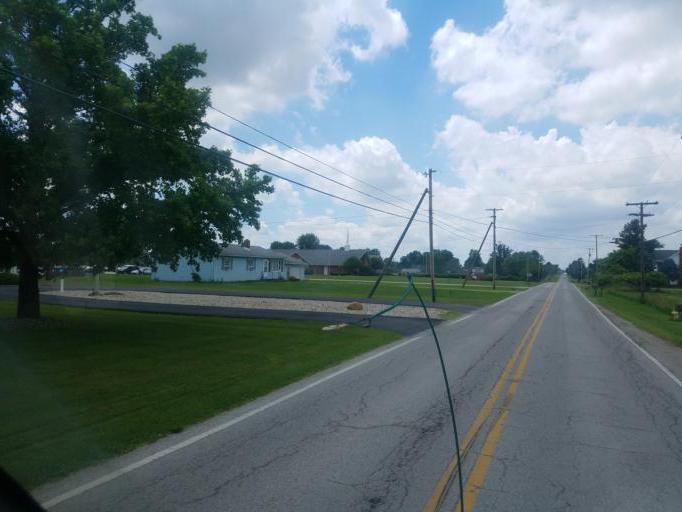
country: US
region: Ohio
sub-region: Huron County
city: Willard
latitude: 41.0546
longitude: -82.7493
